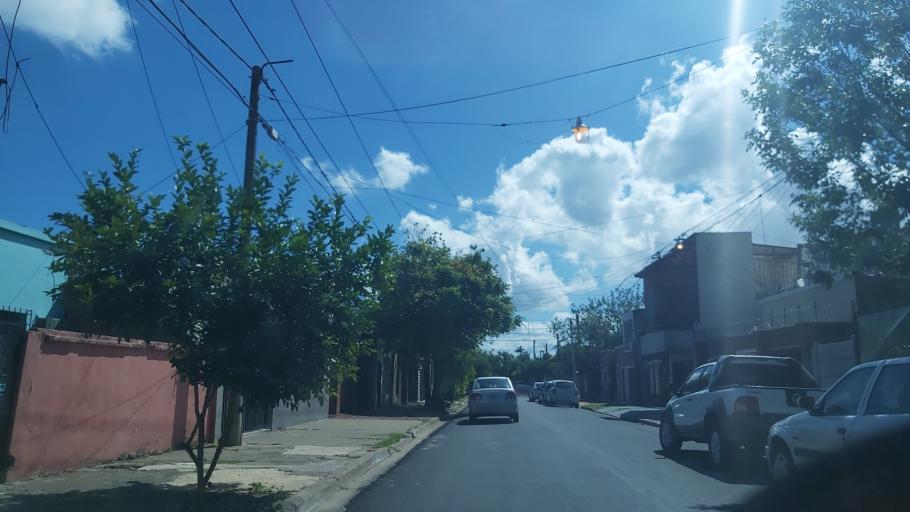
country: AR
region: Corrientes
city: Corrientes
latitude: -27.4777
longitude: -58.8461
